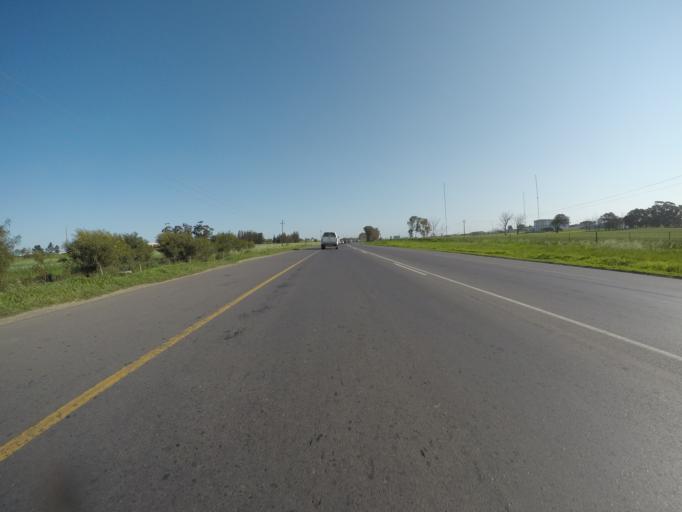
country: ZA
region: Western Cape
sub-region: City of Cape Town
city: Kraaifontein
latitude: -33.7847
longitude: 18.7033
